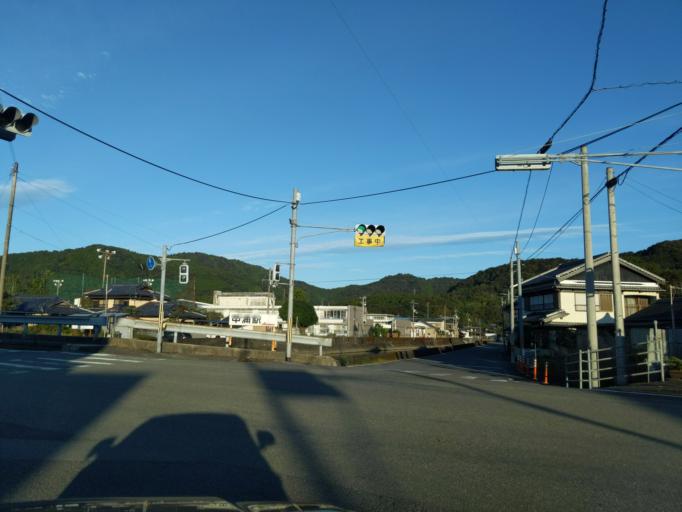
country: JP
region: Kochi
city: Muroto-misakicho
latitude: 33.5443
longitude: 134.2963
